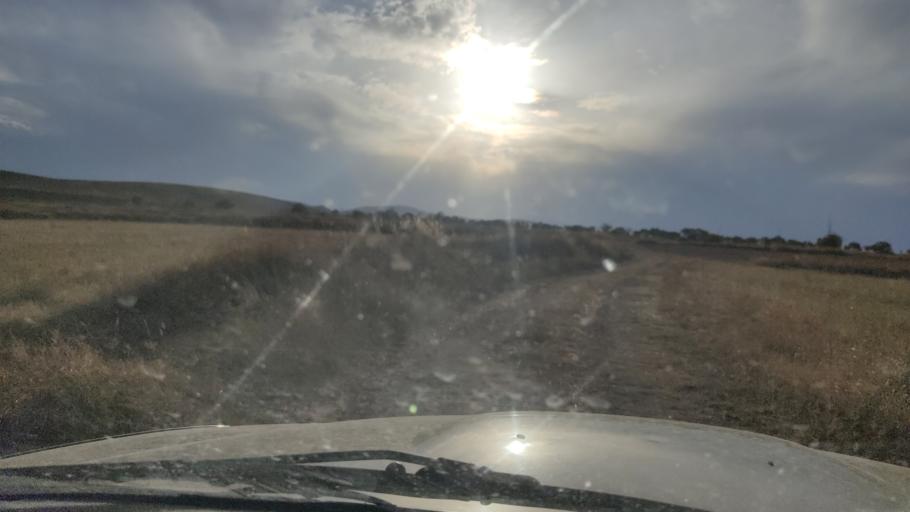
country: ES
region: Aragon
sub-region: Provincia de Teruel
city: Monforte de Moyuela
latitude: 41.0659
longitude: -0.9795
